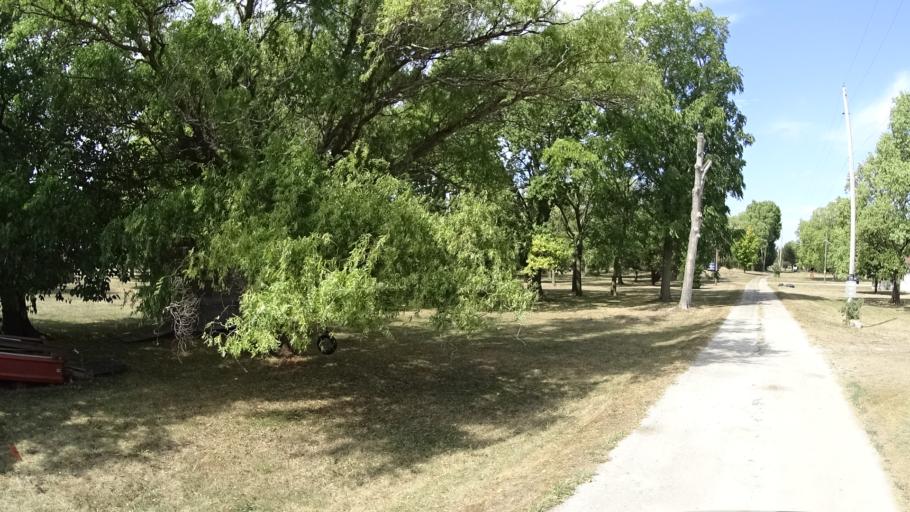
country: US
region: Ohio
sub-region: Erie County
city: Sandusky
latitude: 41.5965
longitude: -82.7022
